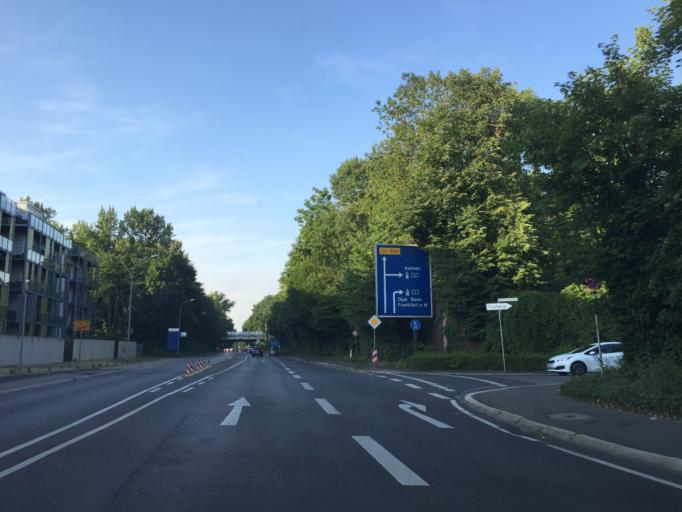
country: DE
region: North Rhine-Westphalia
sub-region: Regierungsbezirk Koln
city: Hurth
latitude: 50.8958
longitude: 6.9067
